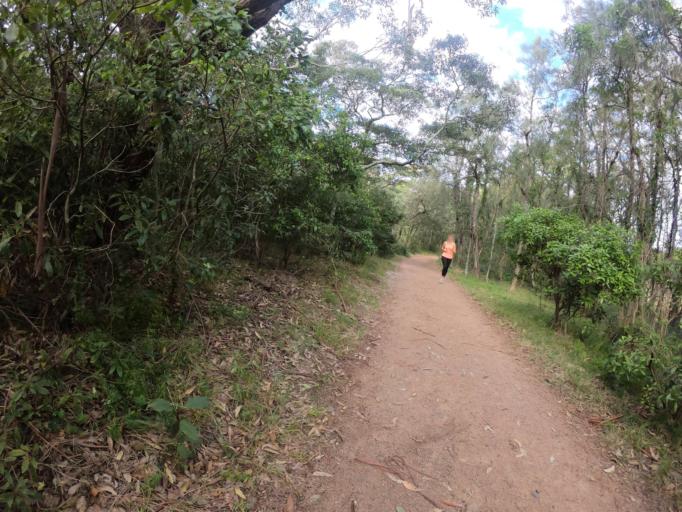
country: AU
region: New South Wales
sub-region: Wollongong
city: Fairy Meadow
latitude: -34.4053
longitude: 150.9009
